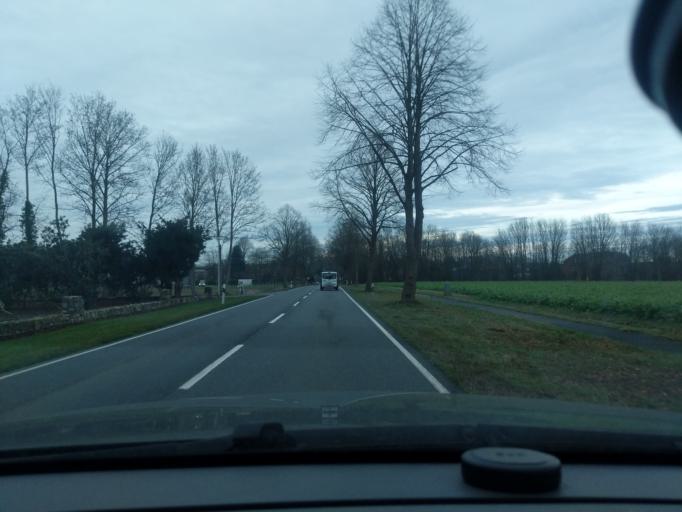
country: DE
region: Lower Saxony
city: Beckdorf
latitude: 53.4064
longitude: 9.6102
